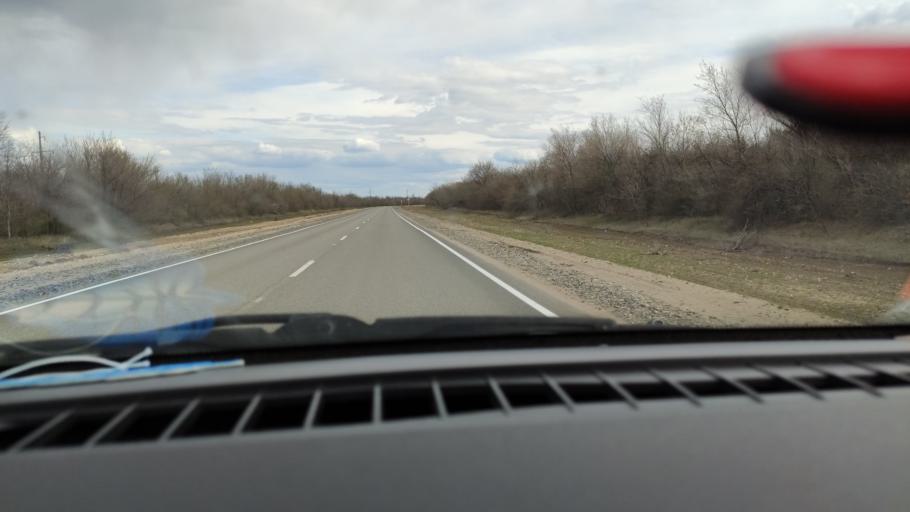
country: RU
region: Saratov
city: Privolzhskiy
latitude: 51.1580
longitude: 45.9605
